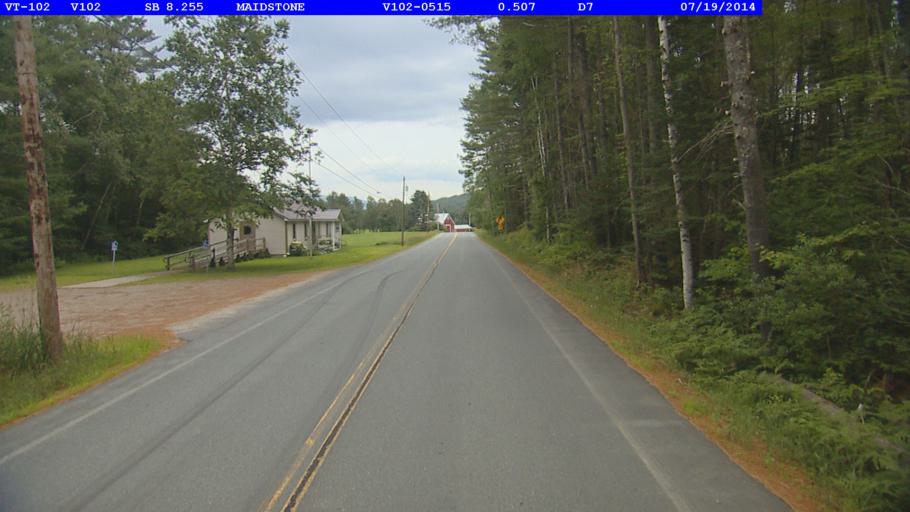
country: US
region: Vermont
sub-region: Essex County
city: Guildhall
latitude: 44.5780
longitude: -71.5551
